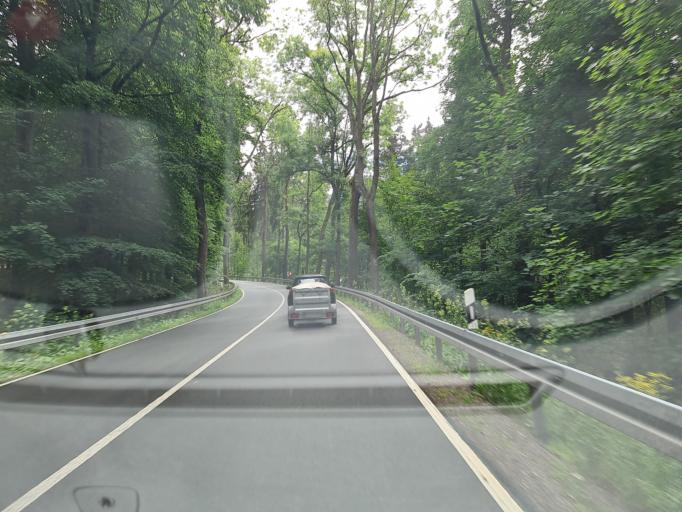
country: DE
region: Saxony
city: Neuhausen
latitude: 50.6970
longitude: 13.4504
